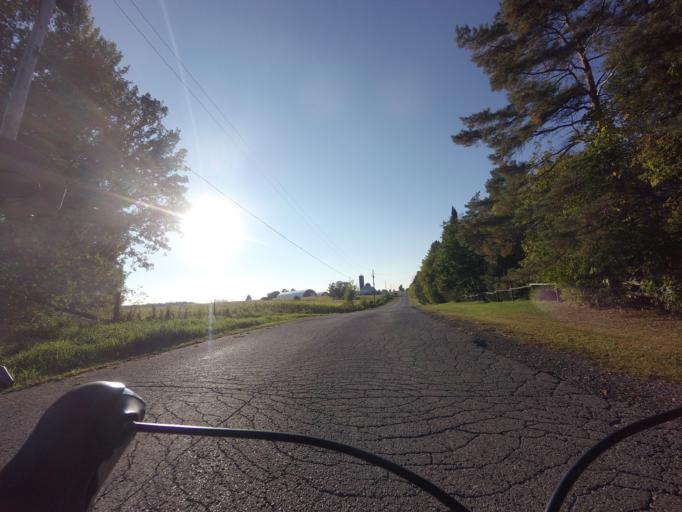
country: CA
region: Ontario
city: Bells Corners
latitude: 45.2249
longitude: -75.7209
